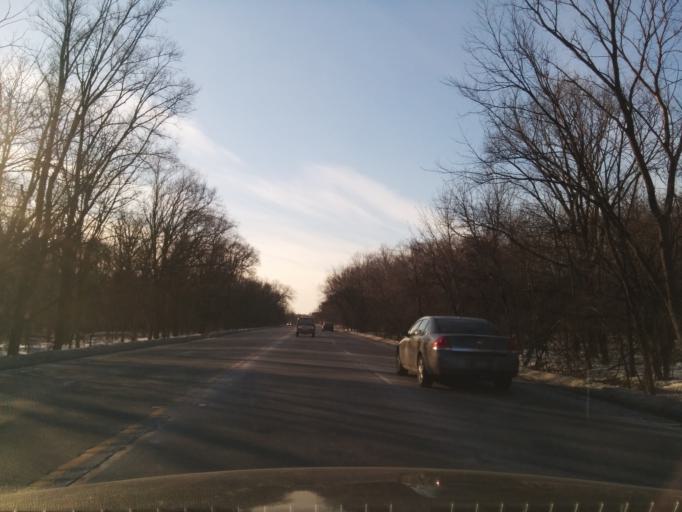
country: US
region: Illinois
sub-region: Cook County
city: Norridge
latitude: 41.9527
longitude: -87.8476
